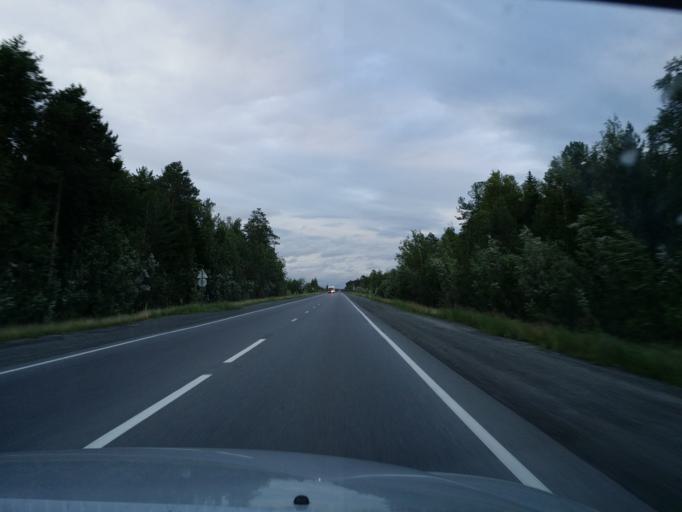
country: RU
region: Khanty-Mansiyskiy Avtonomnyy Okrug
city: Surgut
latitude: 61.3409
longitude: 73.5875
